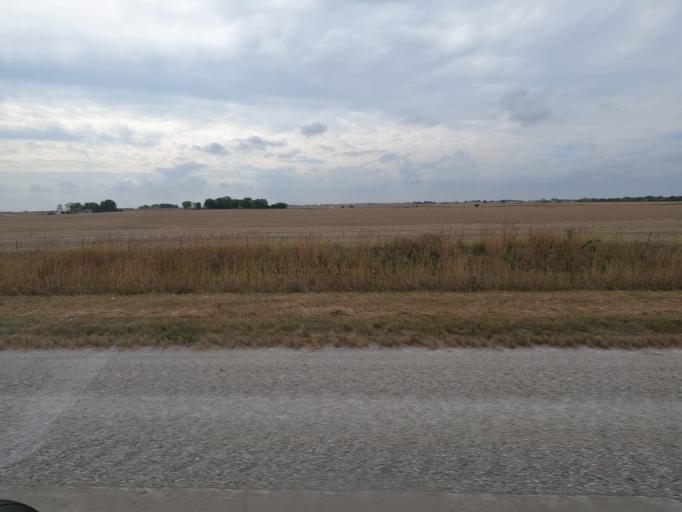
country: US
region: Iowa
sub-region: Jasper County
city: Monroe
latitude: 41.4924
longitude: -93.0732
